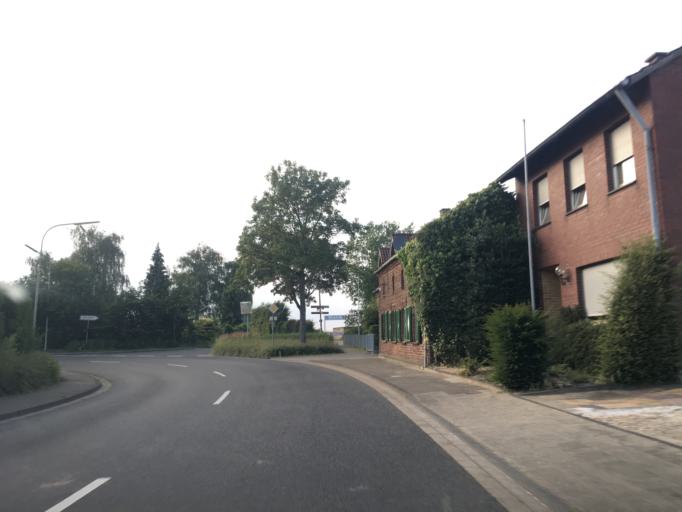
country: DE
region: North Rhine-Westphalia
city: Huckelhoven
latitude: 51.0787
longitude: 6.2179
